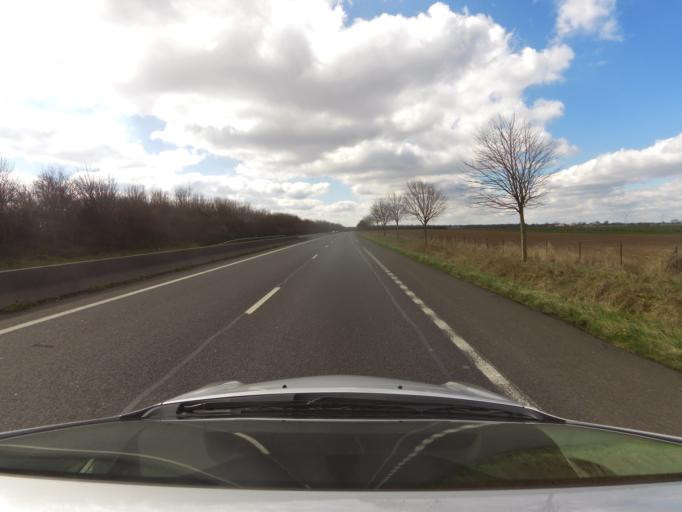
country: FR
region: Picardie
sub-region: Departement de la Somme
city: Bouttencourt
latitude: 49.9786
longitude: 1.6765
